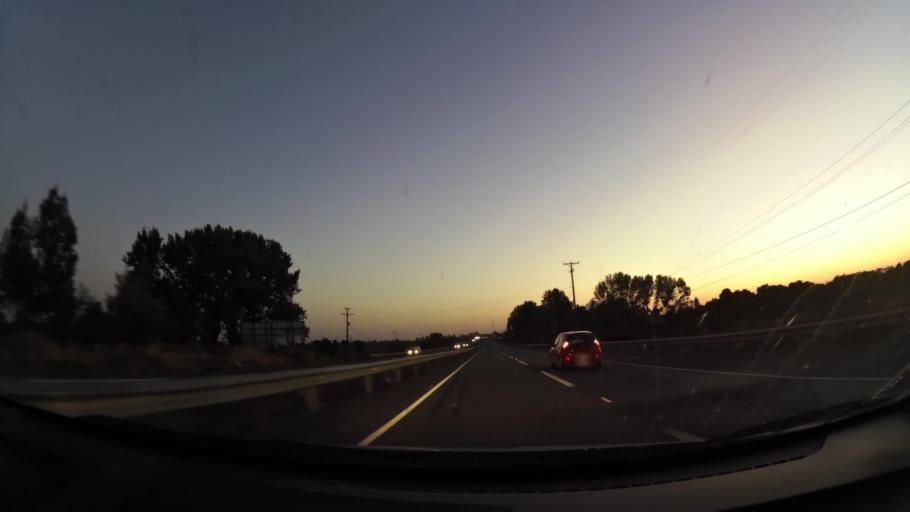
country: CL
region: Maule
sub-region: Provincia de Linares
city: Parral
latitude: -36.1846
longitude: -71.8251
